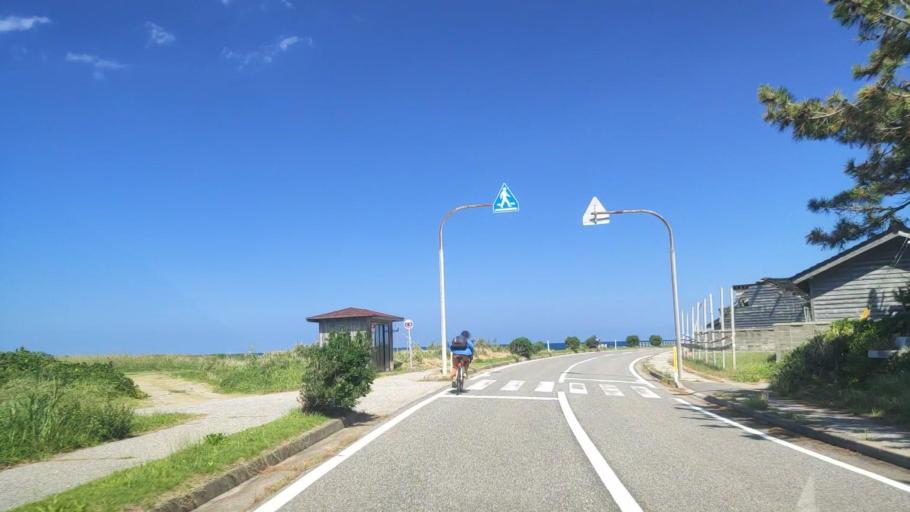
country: JP
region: Ishikawa
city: Nanao
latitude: 37.4834
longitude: 137.1078
